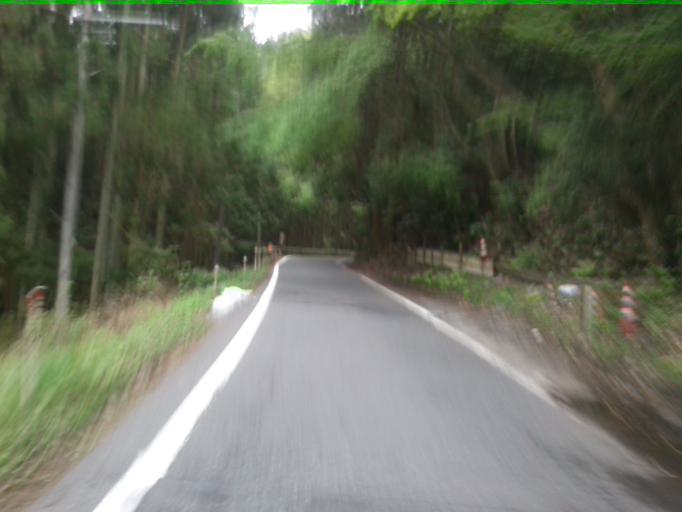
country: JP
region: Kyoto
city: Kameoka
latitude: 34.9580
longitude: 135.5562
